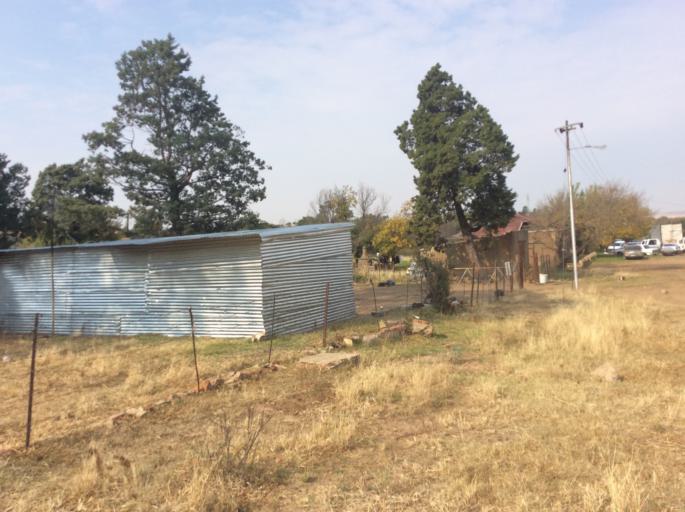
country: LS
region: Mafeteng
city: Mafeteng
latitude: -29.7241
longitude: 27.0434
